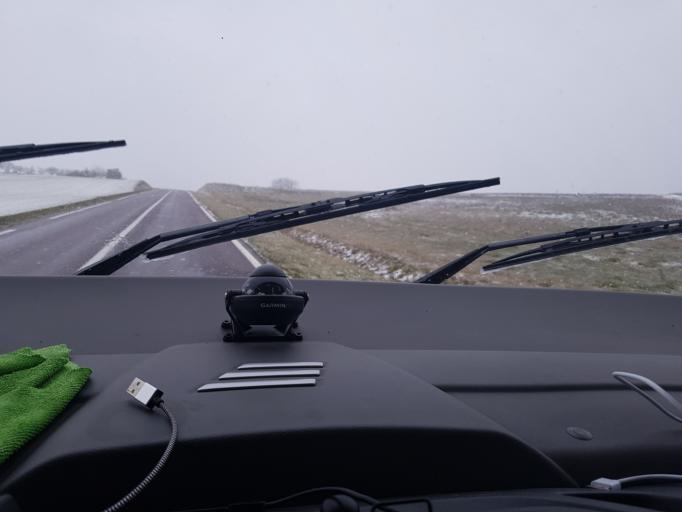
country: FR
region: Lorraine
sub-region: Departement de la Moselle
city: Dieuze
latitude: 48.7274
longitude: 6.7078
